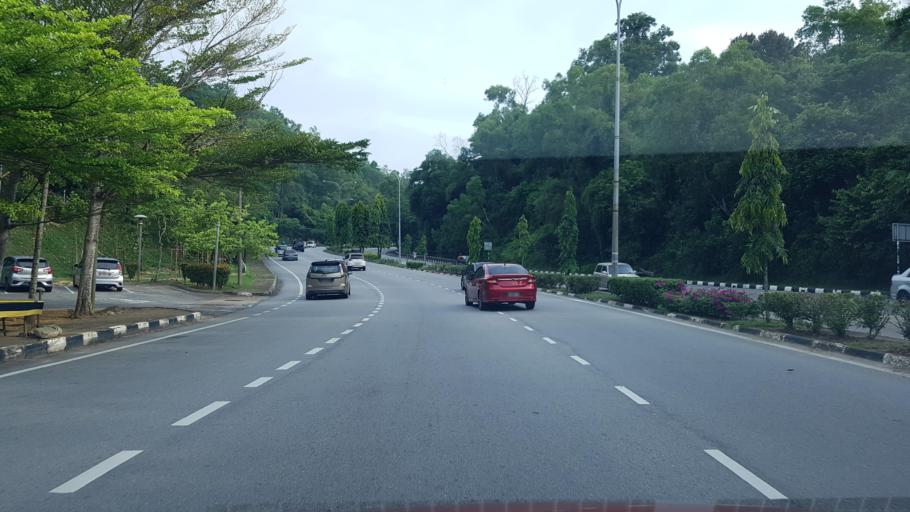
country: MY
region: Terengganu
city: Kuala Terengganu
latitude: 5.3241
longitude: 103.1364
